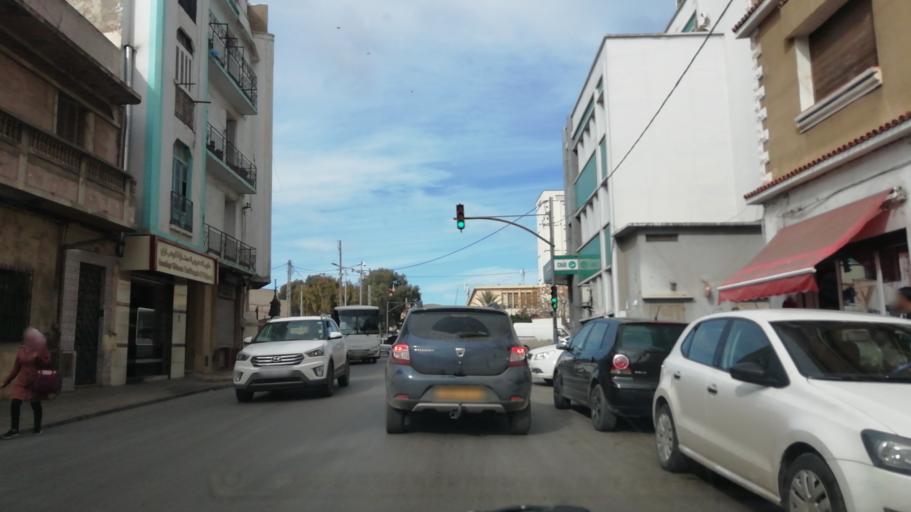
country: DZ
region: Oran
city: Oran
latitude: 35.6935
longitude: -0.6316
